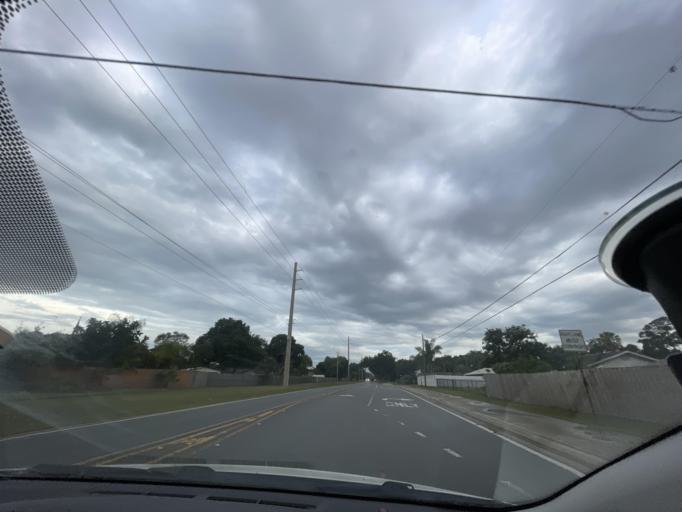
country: US
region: Florida
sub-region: Volusia County
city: Port Orange
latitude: 29.1044
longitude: -80.9932
